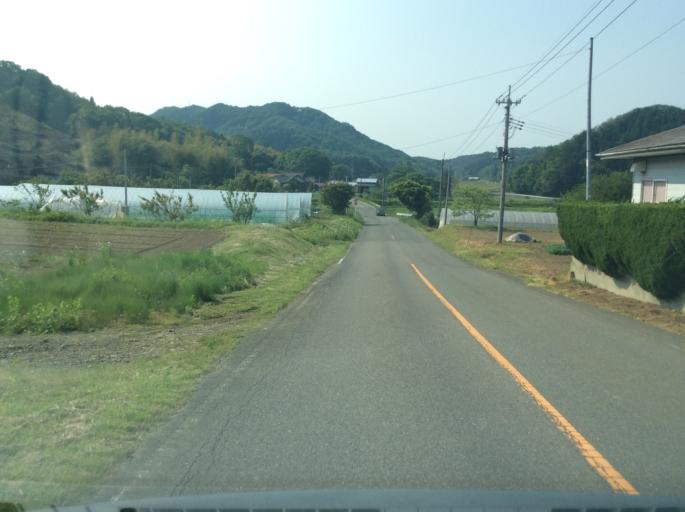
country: JP
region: Tochigi
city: Kuroiso
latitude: 37.0574
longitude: 140.2343
